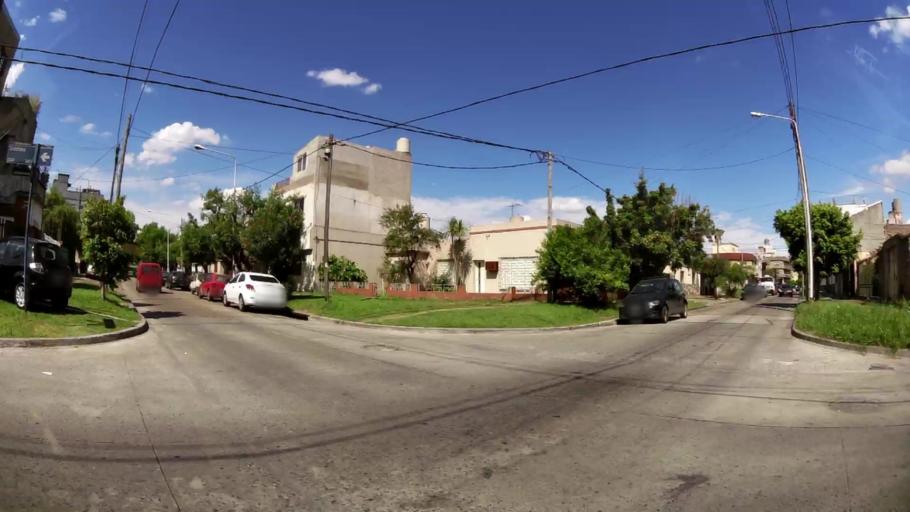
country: AR
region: Buenos Aires
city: San Justo
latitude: -34.6565
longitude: -58.5281
